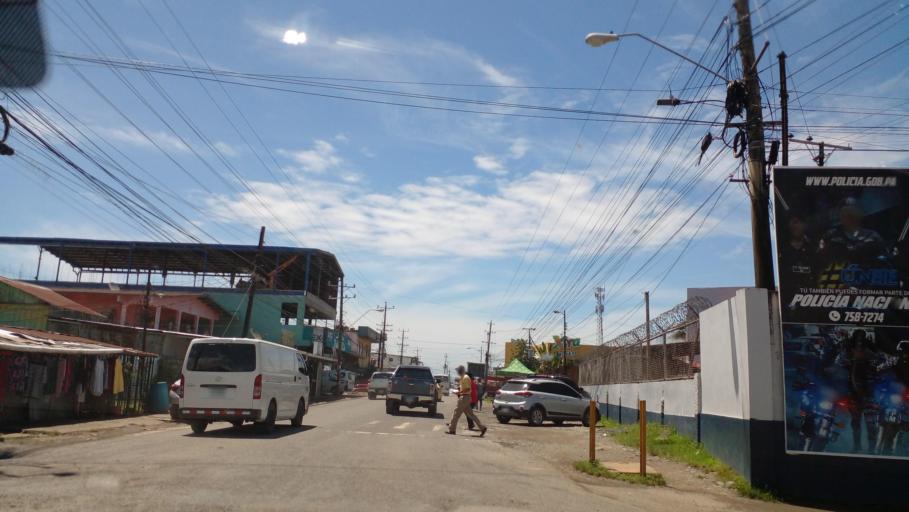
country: PA
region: Bocas del Toro
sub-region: Distrito de Changuinola
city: Changuinola
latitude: 9.4481
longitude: -82.5186
